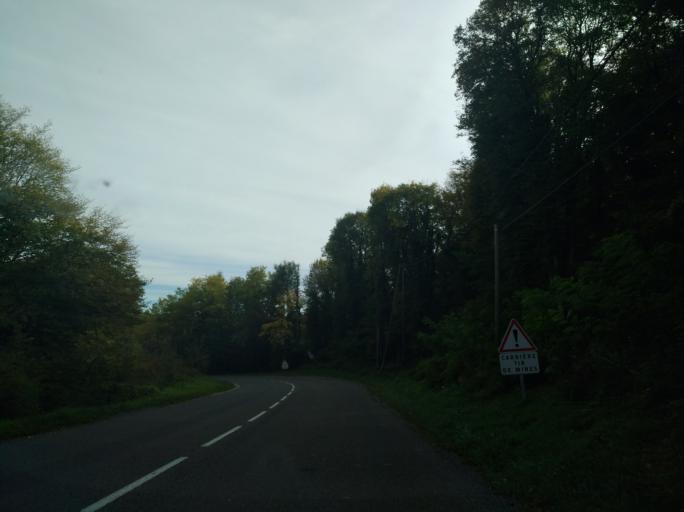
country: FR
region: Bourgogne
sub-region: Departement de Saone-et-Loire
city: Cuiseaux
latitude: 46.4609
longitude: 5.4031
